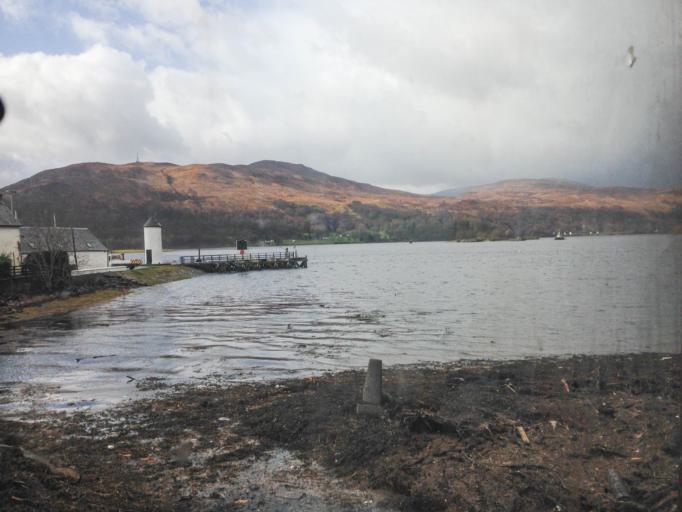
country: GB
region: Scotland
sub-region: Highland
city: Fort William
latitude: 56.8428
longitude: -5.1232
